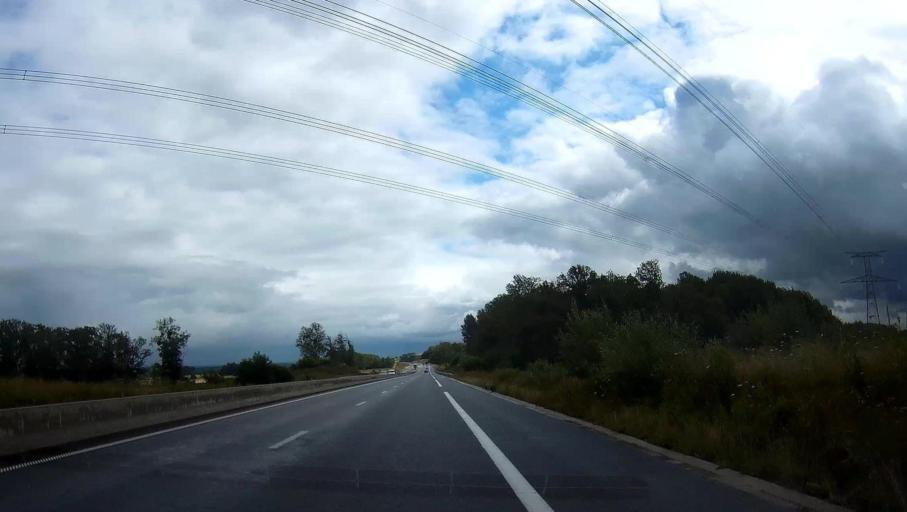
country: FR
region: Champagne-Ardenne
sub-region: Departement des Ardennes
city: Rimogne
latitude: 49.7885
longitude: 4.5632
